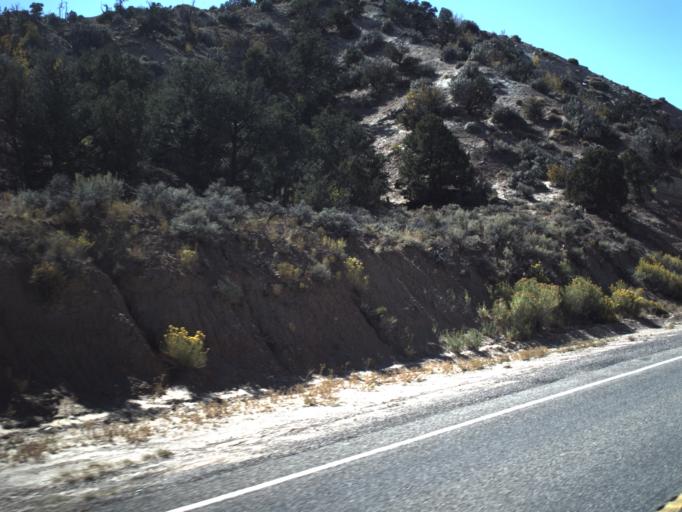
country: US
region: Utah
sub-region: Garfield County
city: Panguitch
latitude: 37.5637
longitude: -112.0368
